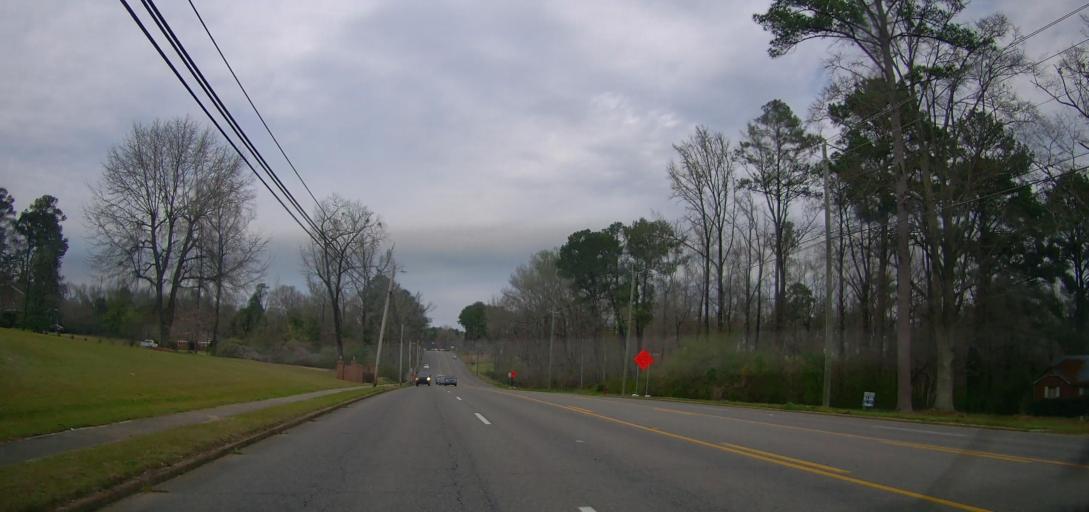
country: US
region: Alabama
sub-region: Marion County
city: Hamilton
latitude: 34.1281
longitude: -87.9900
